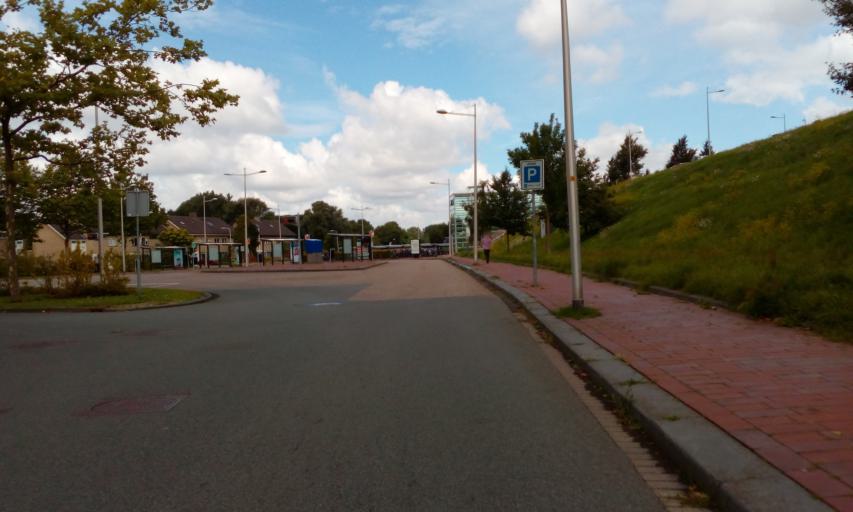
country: NL
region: South Holland
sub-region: Gemeente Barendrecht
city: Barendrecht
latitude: 51.8543
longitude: 4.5524
